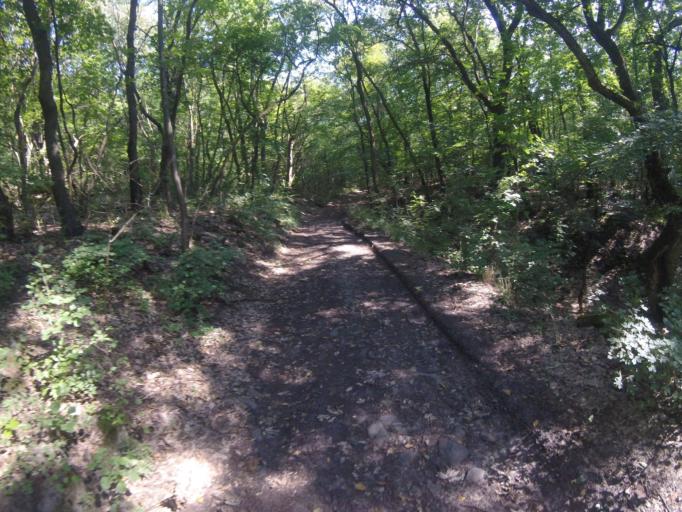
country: HU
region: Nograd
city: Bujak
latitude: 47.8928
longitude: 19.5391
